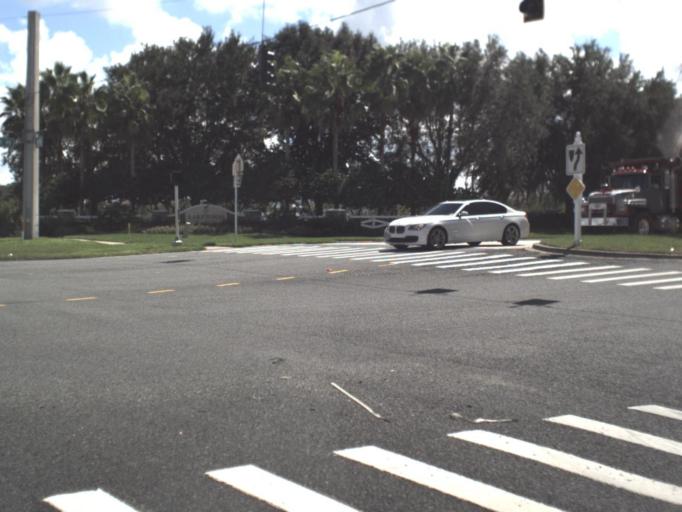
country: US
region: Florida
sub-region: Sarasota County
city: The Meadows
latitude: 27.4318
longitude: -82.3956
